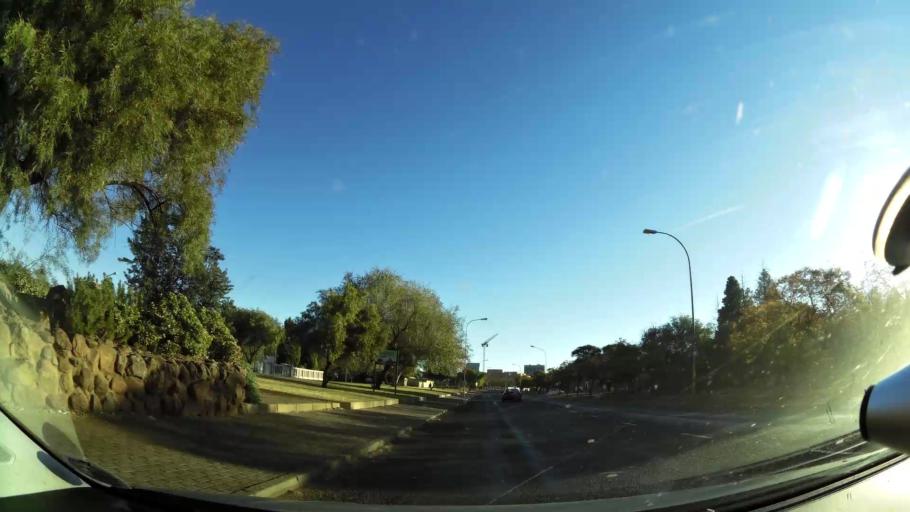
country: ZA
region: Northern Cape
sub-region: Frances Baard District Municipality
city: Kimberley
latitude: -28.7534
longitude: 24.7652
